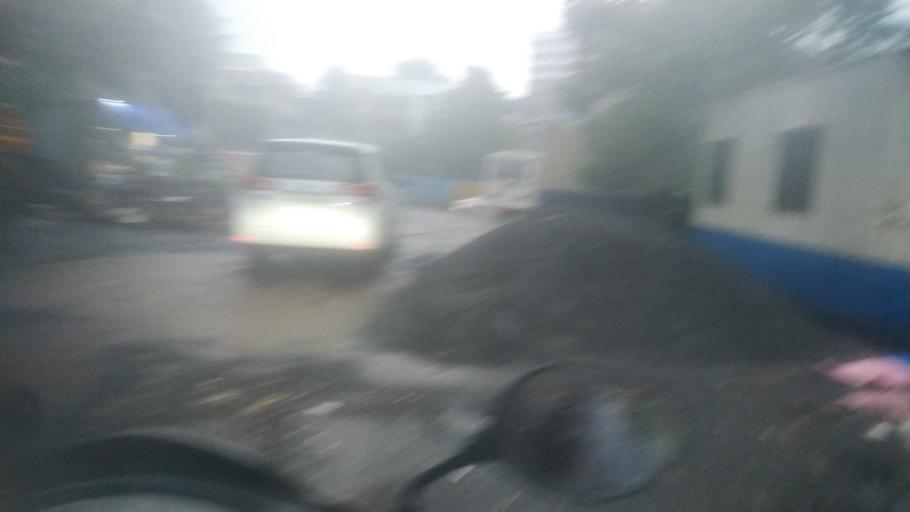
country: IN
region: Maharashtra
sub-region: Mumbai Suburban
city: Mumbai
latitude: 19.1142
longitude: 72.8534
